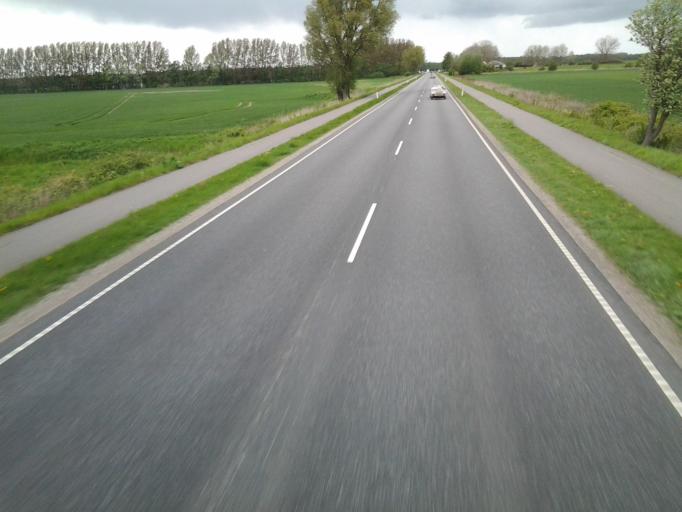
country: DK
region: Zealand
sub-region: Guldborgsund Kommune
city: Nykobing Falster
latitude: 54.7211
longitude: 11.9218
